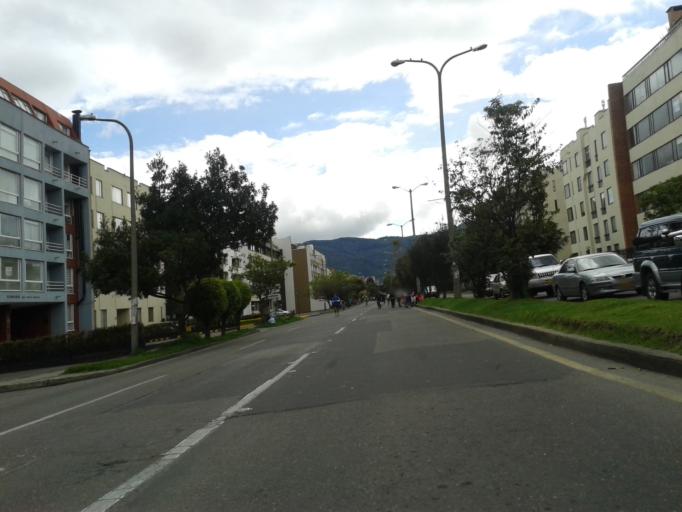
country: CO
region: Bogota D.C.
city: Barrio San Luis
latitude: 4.7007
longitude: -74.0621
